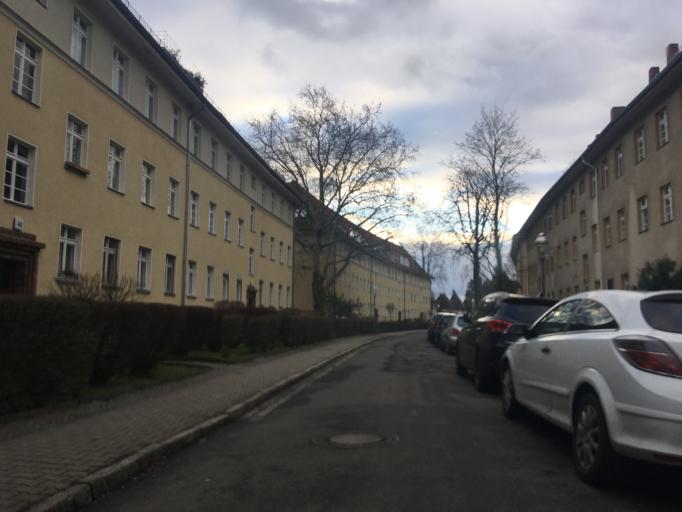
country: DE
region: Berlin
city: Wittenau
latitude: 52.5861
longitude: 13.3333
